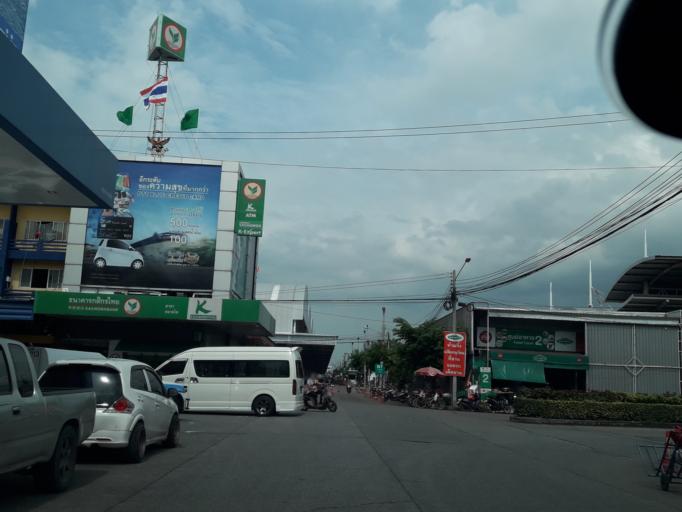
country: TH
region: Pathum Thani
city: Khlong Luang
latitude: 14.0824
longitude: 100.6262
